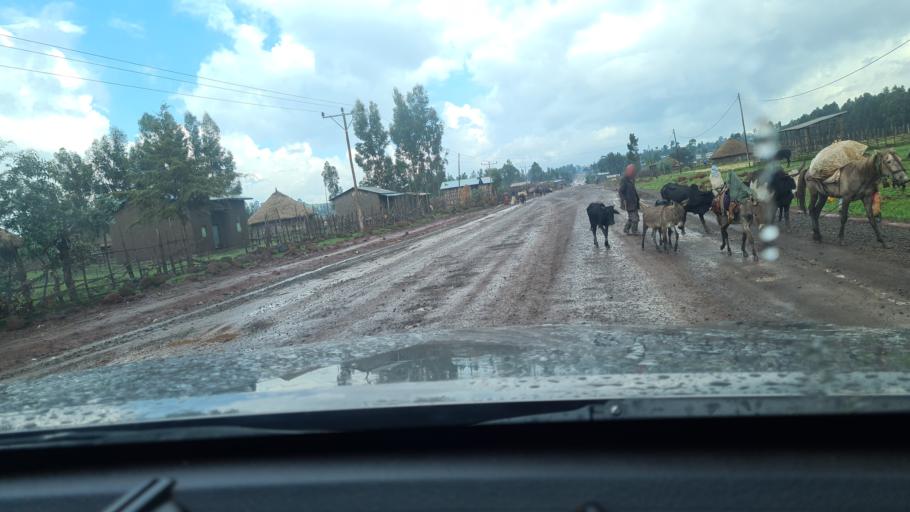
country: ET
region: Oromiya
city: Huruta
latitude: 8.0752
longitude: 39.5462
